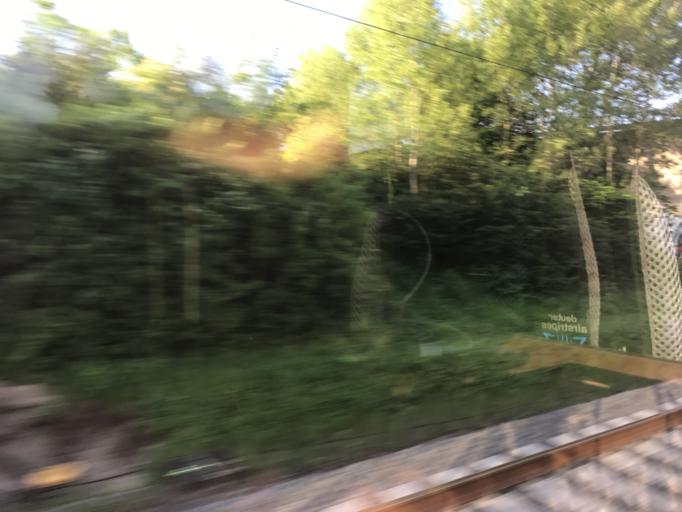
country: DE
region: Hesse
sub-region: Regierungsbezirk Darmstadt
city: Eltville
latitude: 50.0015
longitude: 8.1263
